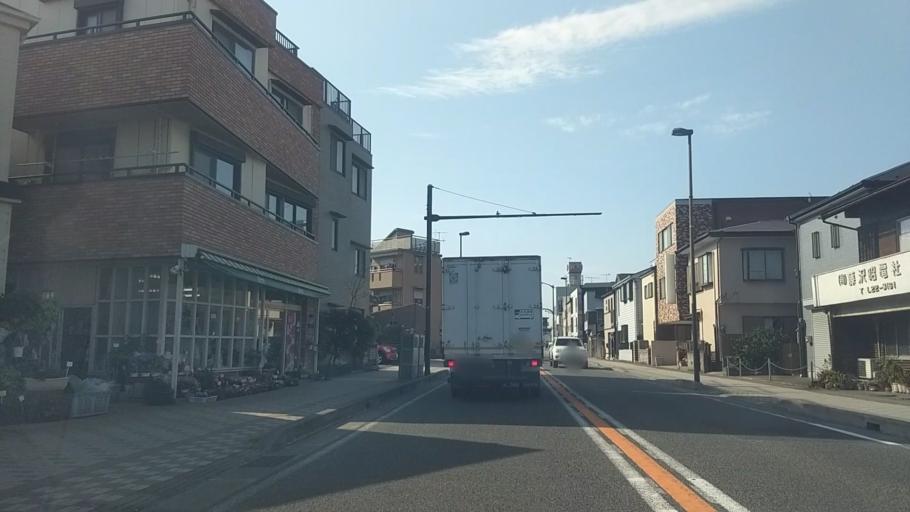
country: JP
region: Kanagawa
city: Fujisawa
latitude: 35.3439
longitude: 139.4876
